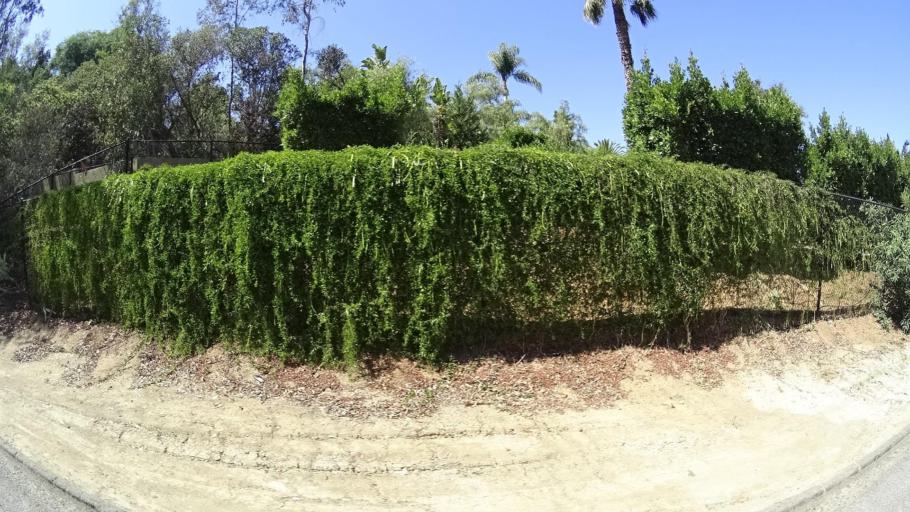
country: US
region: California
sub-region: San Diego County
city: Fairbanks Ranch
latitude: 33.0001
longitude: -117.1792
